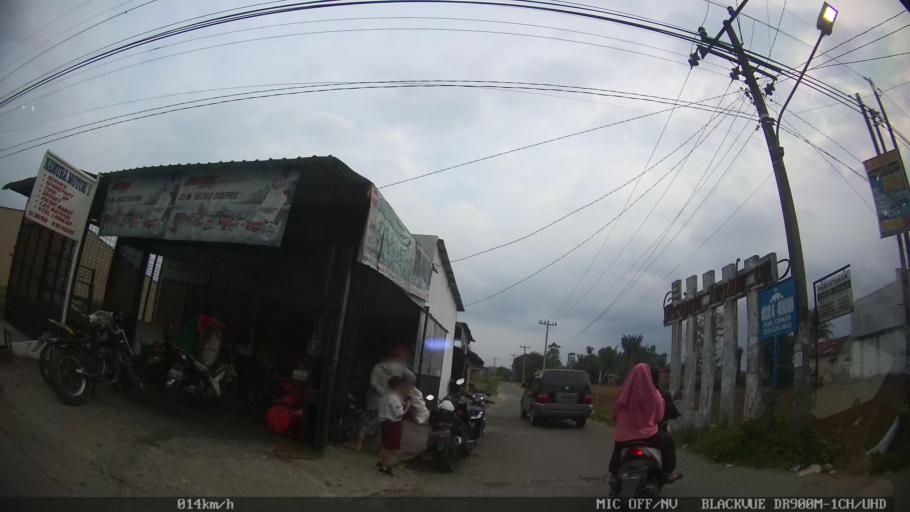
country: ID
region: North Sumatra
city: Sunggal
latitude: 3.5609
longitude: 98.5841
